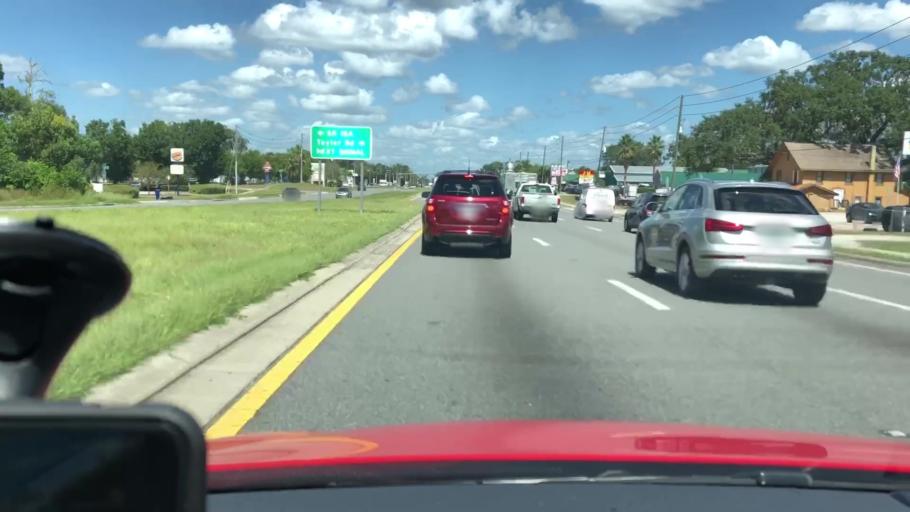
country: US
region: Florida
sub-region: Volusia County
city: De Land Southwest
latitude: 28.9947
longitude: -81.3024
